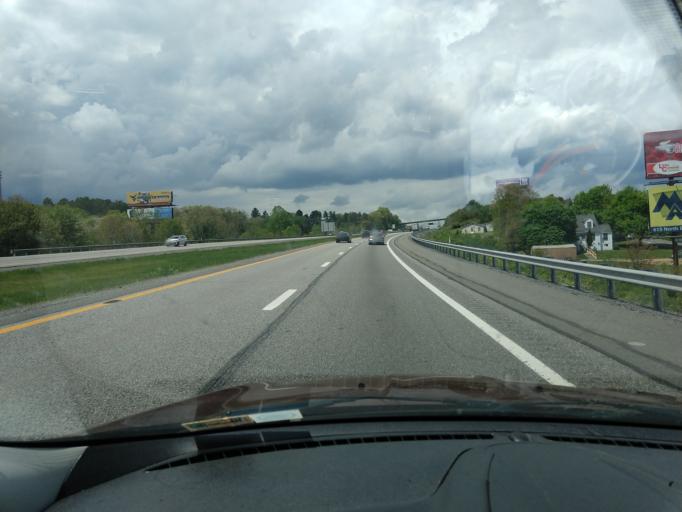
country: US
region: West Virginia
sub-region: Mercer County
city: Athens
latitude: 37.3889
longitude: -81.0554
